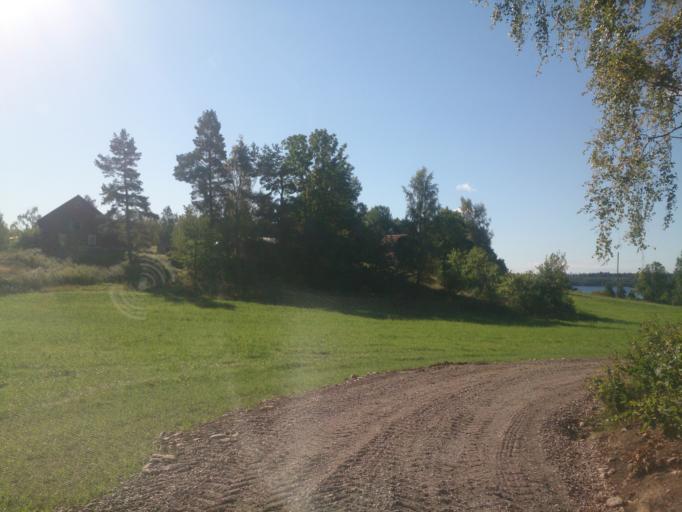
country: SE
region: OEstergoetland
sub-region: Atvidabergs Kommun
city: Atvidaberg
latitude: 58.2606
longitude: 15.9641
